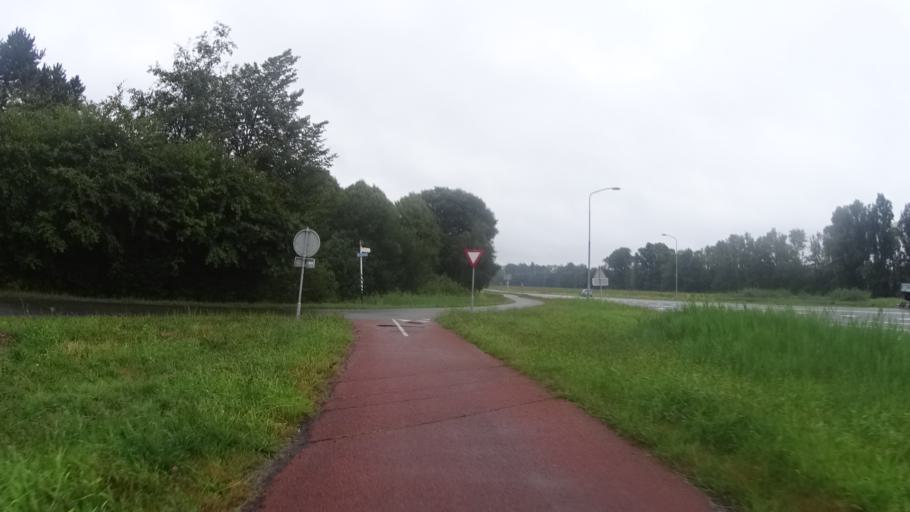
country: NL
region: Groningen
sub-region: Gemeente  Oldambt
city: Winschoten
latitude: 53.1651
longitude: 6.9977
